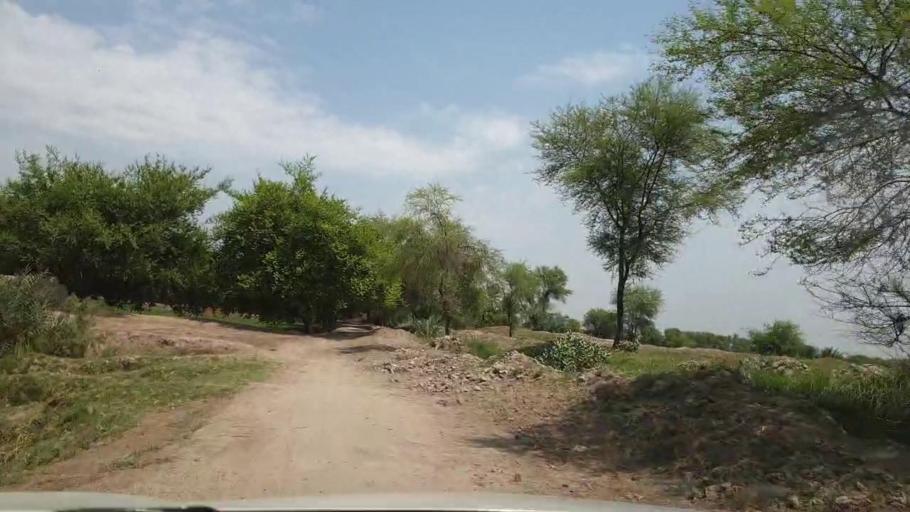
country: PK
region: Sindh
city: Ratodero
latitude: 27.8057
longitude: 68.2320
